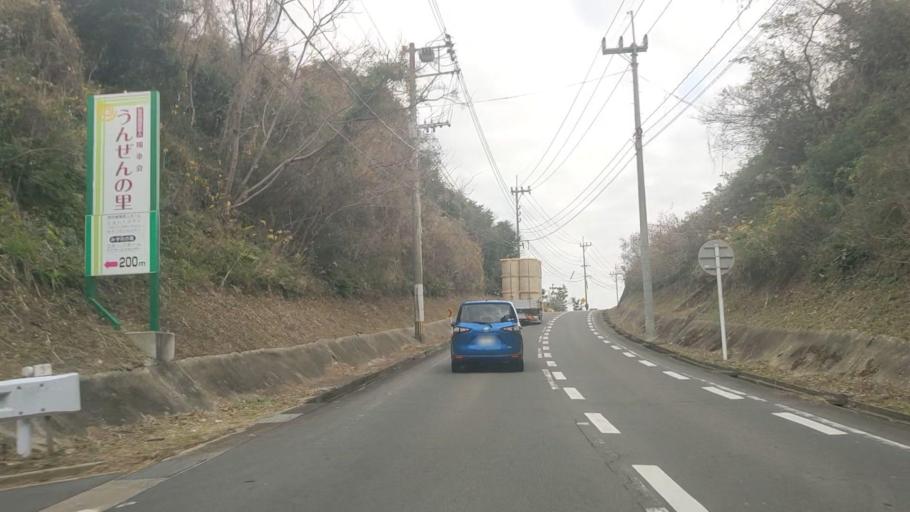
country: JP
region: Nagasaki
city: Shimabara
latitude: 32.8461
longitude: 130.2160
